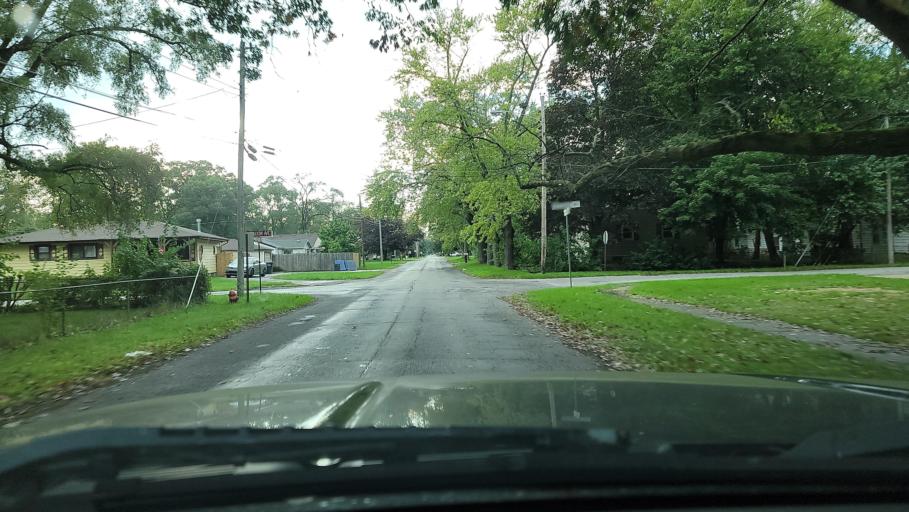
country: US
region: Indiana
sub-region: Lake County
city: Lake Station
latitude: 41.5705
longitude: -87.2144
